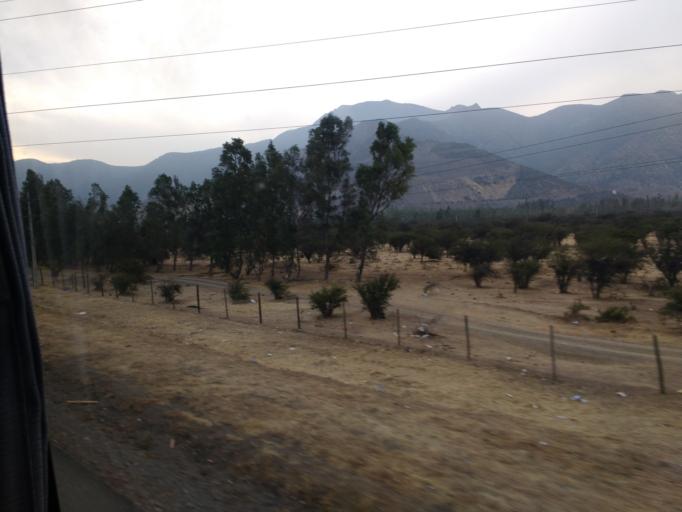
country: CL
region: Santiago Metropolitan
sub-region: Provincia de Talagante
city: Penaflor
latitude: -33.4580
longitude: -70.9061
